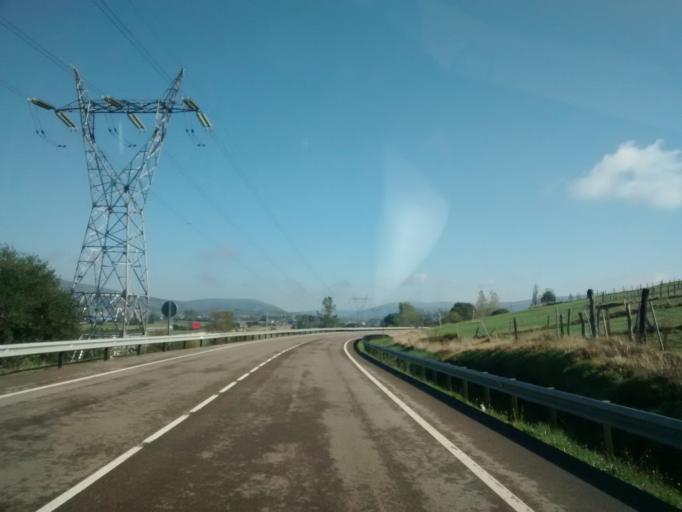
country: ES
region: Cantabria
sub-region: Provincia de Cantabria
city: Reinosa
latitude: 42.9873
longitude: -4.1306
